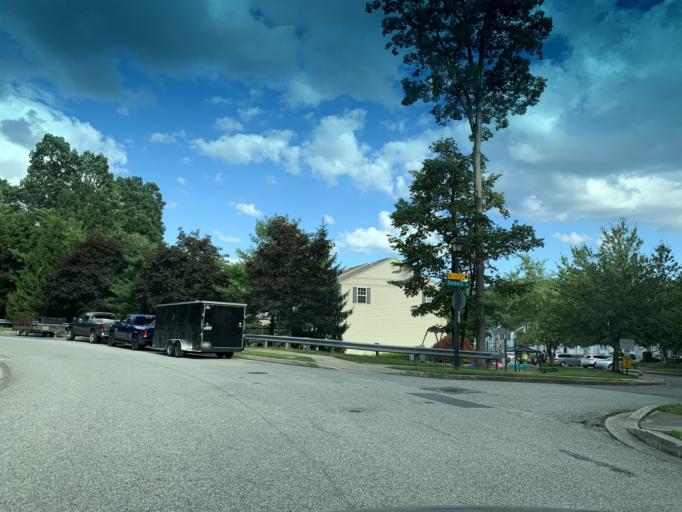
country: US
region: Maryland
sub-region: Harford County
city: Riverside
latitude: 39.4819
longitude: -76.2426
